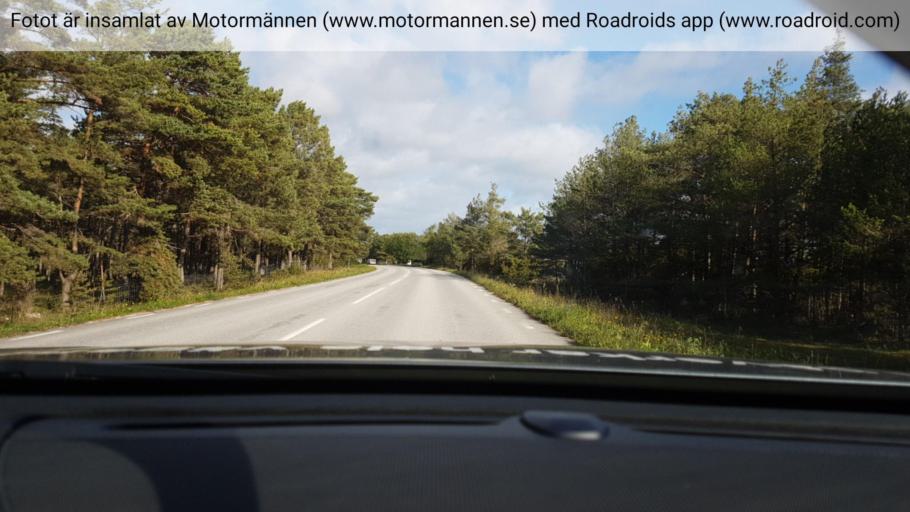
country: SE
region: Gotland
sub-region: Gotland
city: Slite
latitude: 57.8771
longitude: 19.0861
